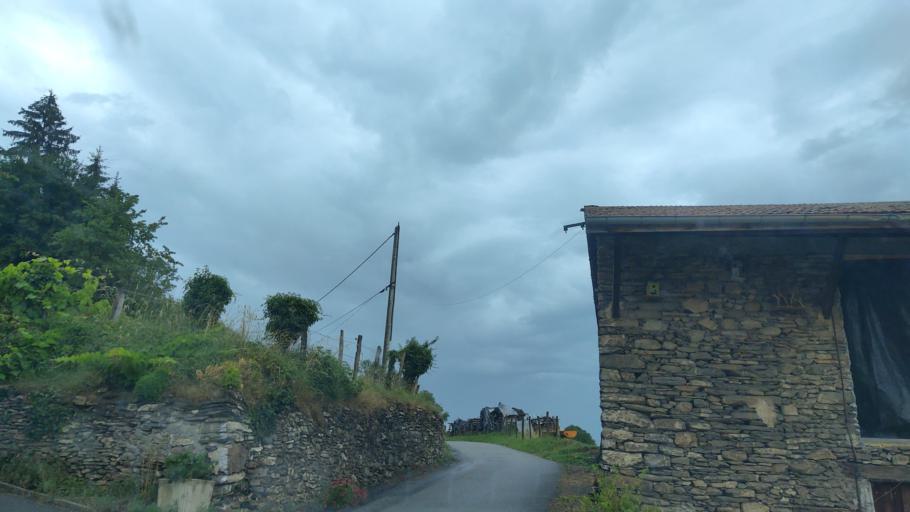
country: FR
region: Rhone-Alpes
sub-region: Departement de la Savoie
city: La Rochette
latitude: 45.4886
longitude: 6.1290
